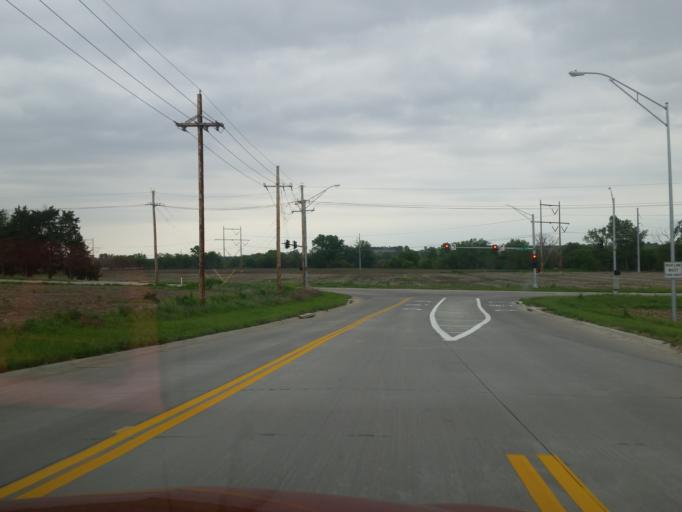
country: US
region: Nebraska
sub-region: Douglas County
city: Bennington
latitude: 41.3199
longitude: -96.1197
